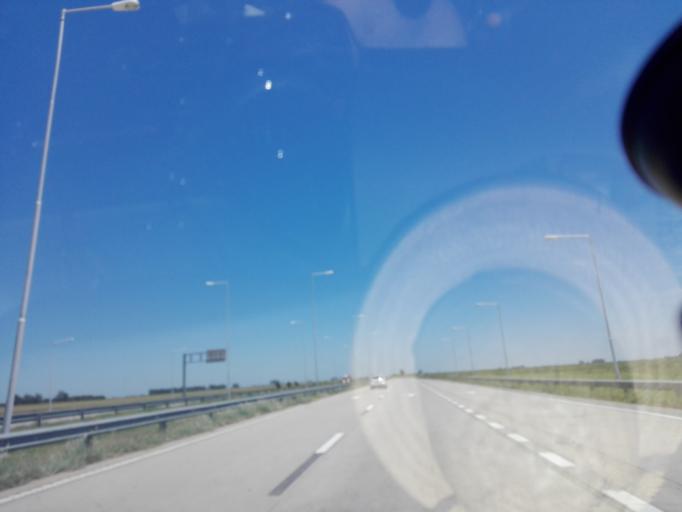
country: AR
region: Cordoba
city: Leones
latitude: -32.6223
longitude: -62.3331
